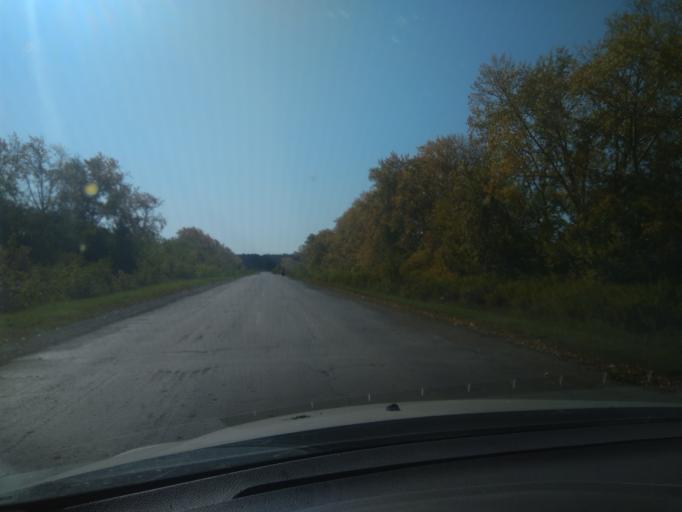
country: RU
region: Sverdlovsk
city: Pokrovskoye
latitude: 56.4584
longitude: 61.6083
